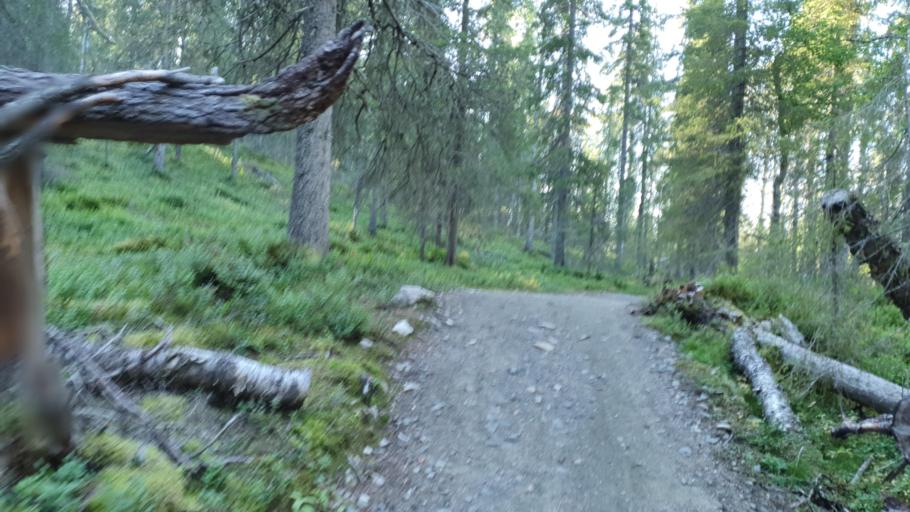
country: FI
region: Lapland
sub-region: Tunturi-Lappi
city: Kolari
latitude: 67.5971
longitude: 24.2175
